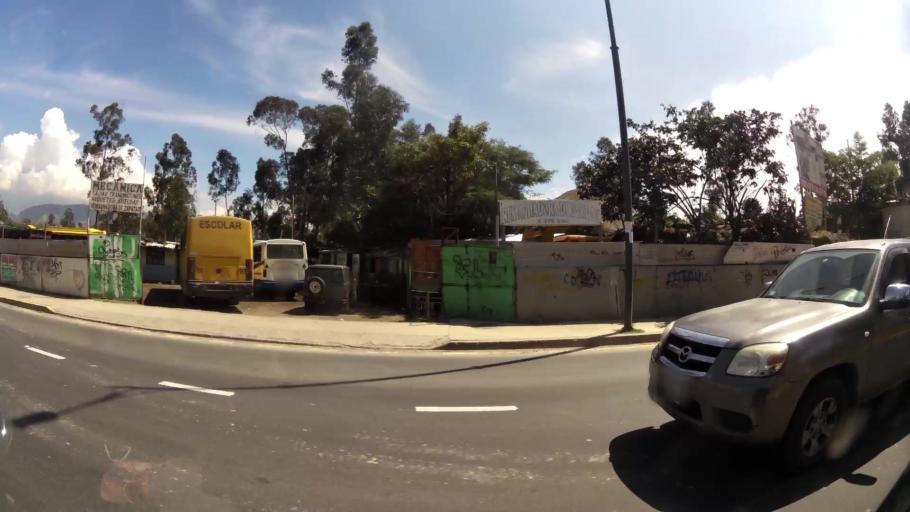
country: EC
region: Pichincha
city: Quito
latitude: -0.2155
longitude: -78.3936
